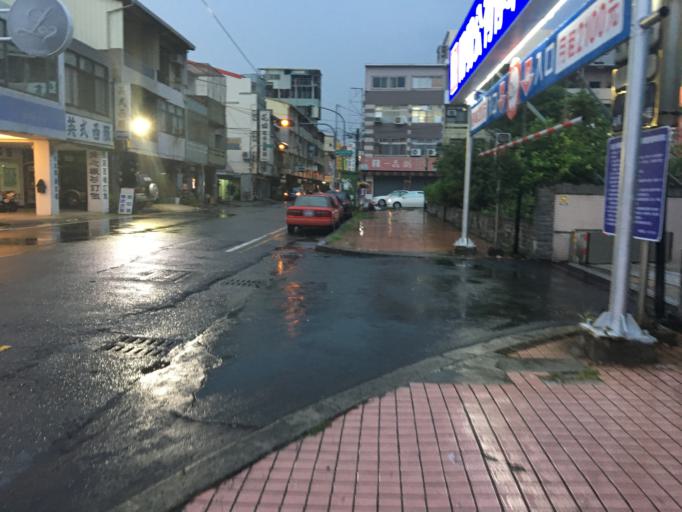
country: TW
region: Taiwan
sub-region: Changhua
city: Chang-hua
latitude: 24.0875
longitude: 120.5498
